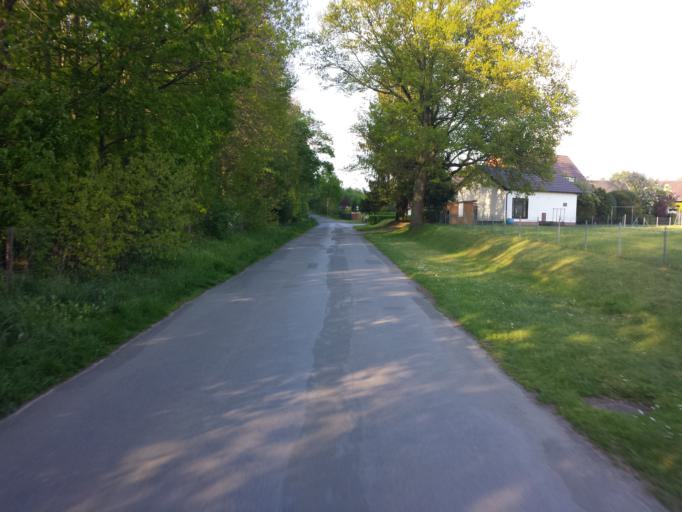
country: DE
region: North Rhine-Westphalia
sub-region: Regierungsbezirk Detmold
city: Rheda-Wiedenbruck
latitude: 51.8634
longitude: 8.3080
